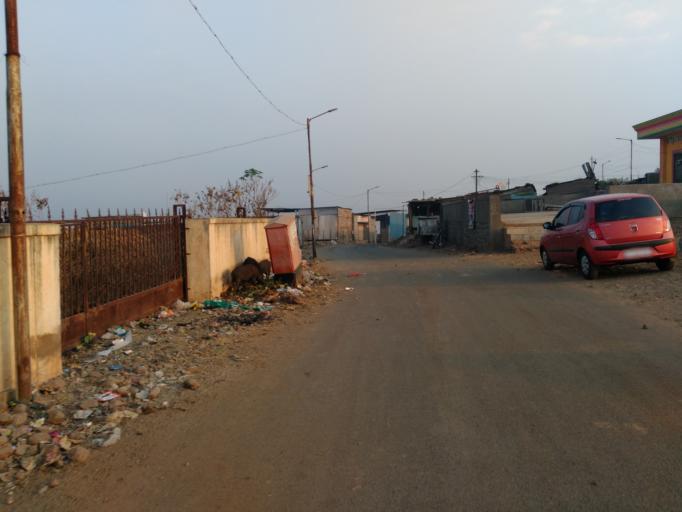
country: IN
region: Maharashtra
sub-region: Pune Division
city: Pune
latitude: 18.4450
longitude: 73.8786
